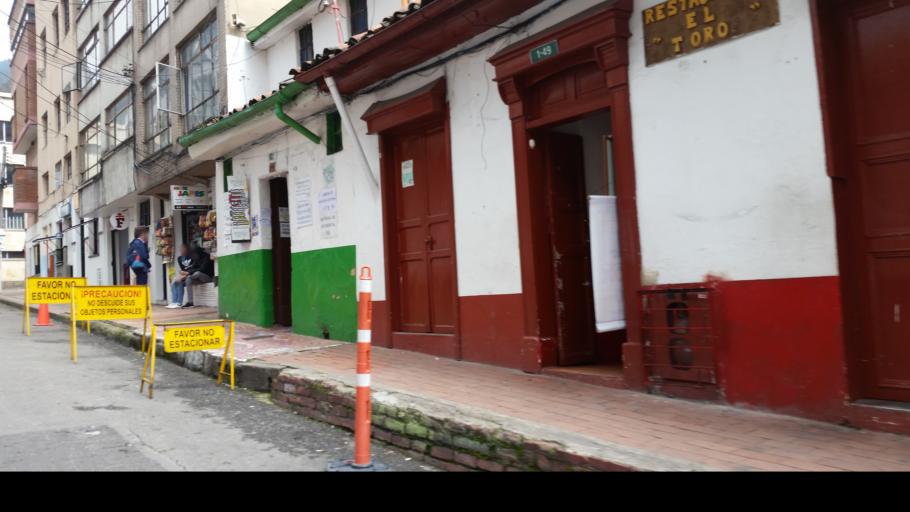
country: CO
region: Bogota D.C.
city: Bogota
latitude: 4.6026
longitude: -74.0667
